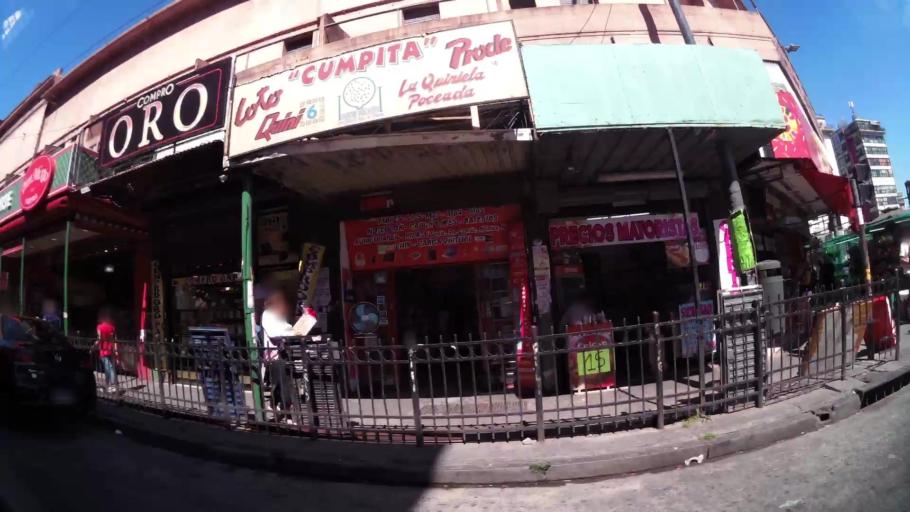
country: AR
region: Buenos Aires F.D.
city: Buenos Aires
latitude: -34.6279
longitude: -58.3814
